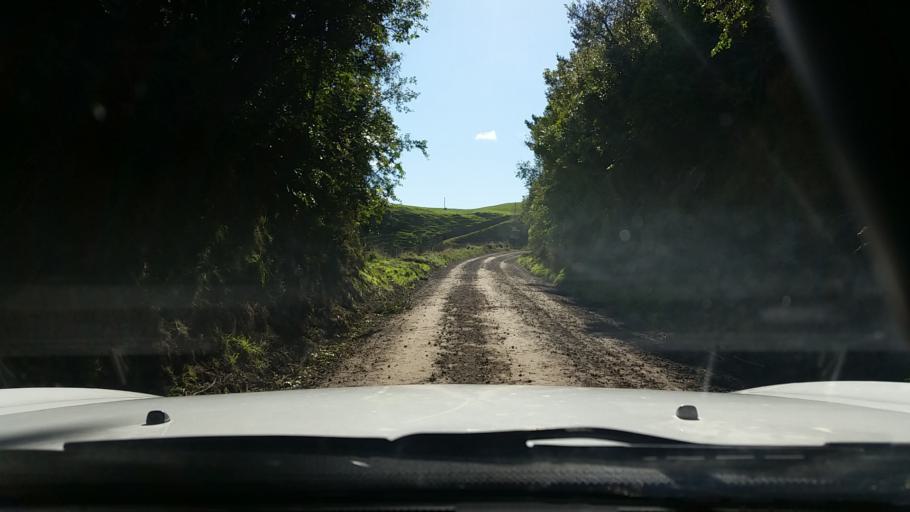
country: NZ
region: Bay of Plenty
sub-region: Rotorua District
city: Rotorua
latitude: -38.3749
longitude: 176.1209
